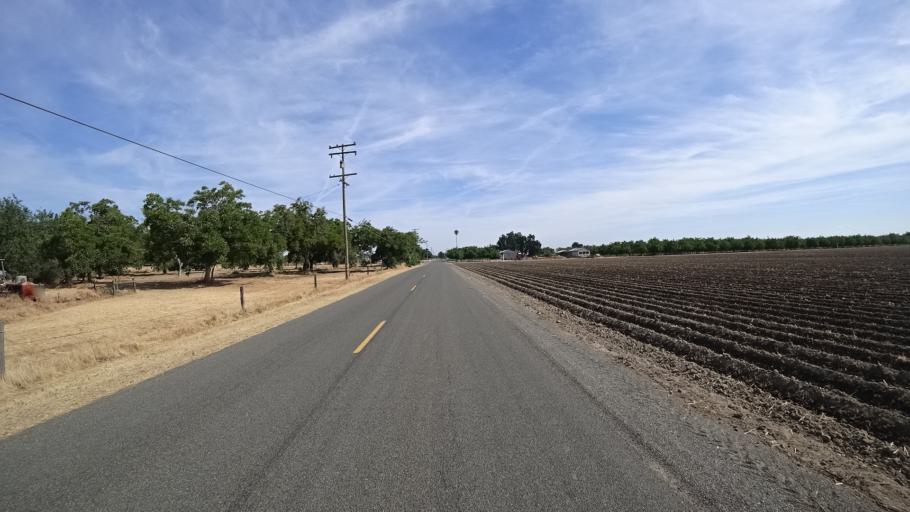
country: US
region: California
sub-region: Kings County
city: Lucerne
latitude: 36.3818
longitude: -119.6100
